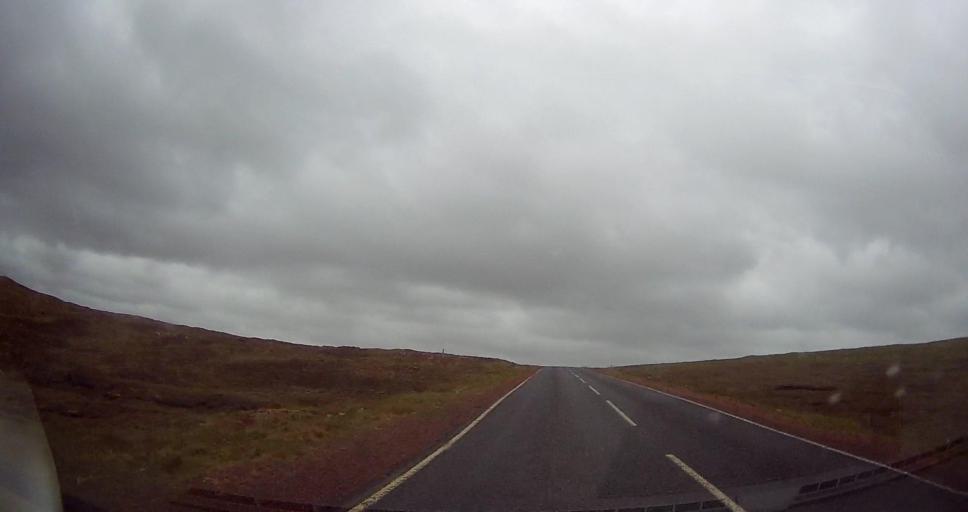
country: GB
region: Scotland
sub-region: Shetland Islands
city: Lerwick
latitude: 60.4830
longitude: -1.4459
